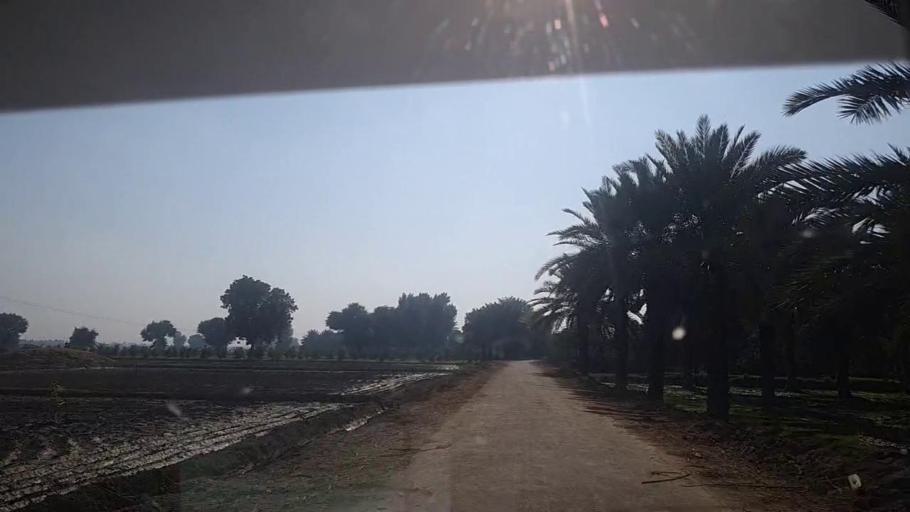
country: PK
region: Sindh
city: Gambat
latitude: 27.3889
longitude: 68.5996
